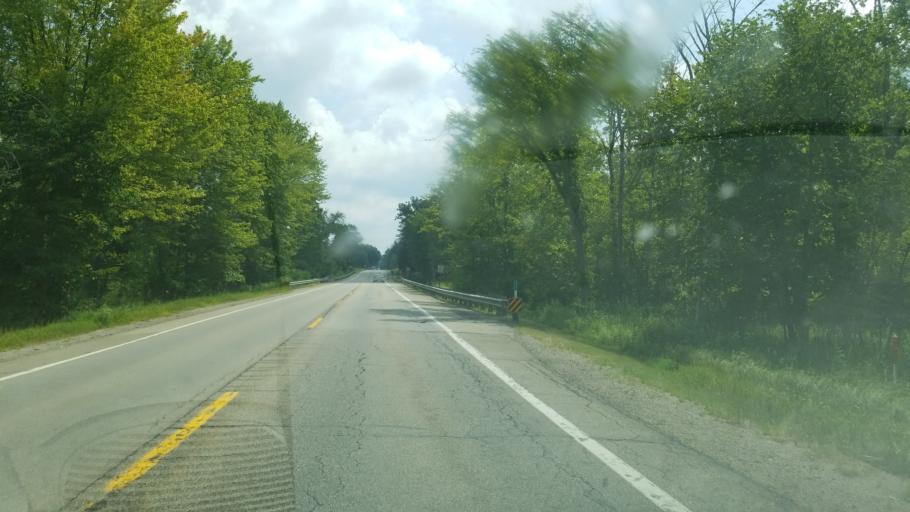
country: US
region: Michigan
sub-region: Kent County
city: Sparta
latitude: 43.2198
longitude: -85.6818
